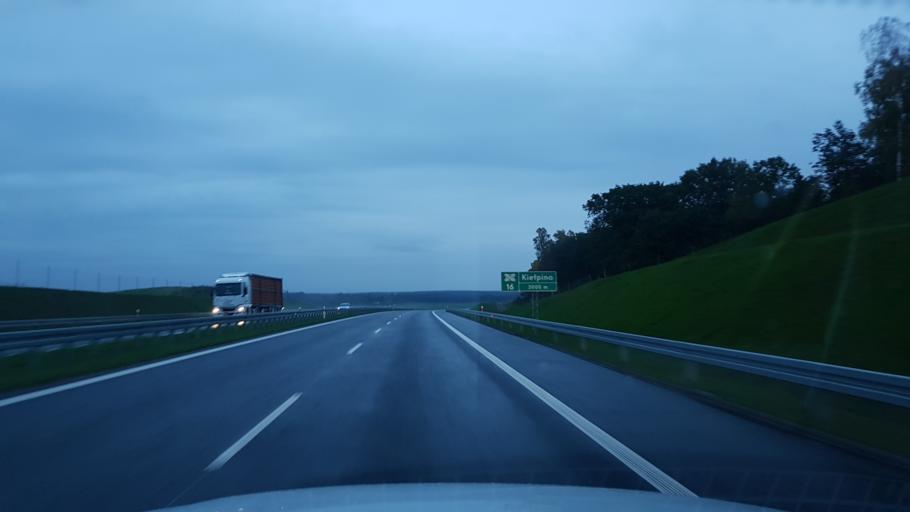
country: PL
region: West Pomeranian Voivodeship
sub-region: Powiat gryficki
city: Brojce
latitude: 53.9132
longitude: 15.3817
